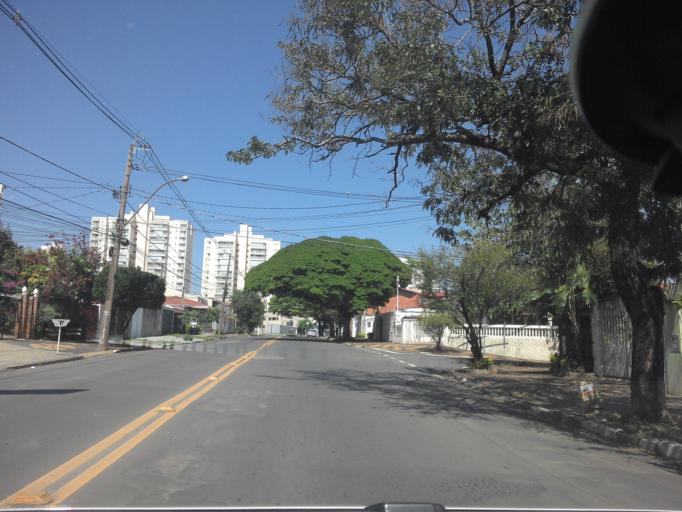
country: BR
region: Sao Paulo
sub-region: Campinas
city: Campinas
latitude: -22.8809
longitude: -47.0595
